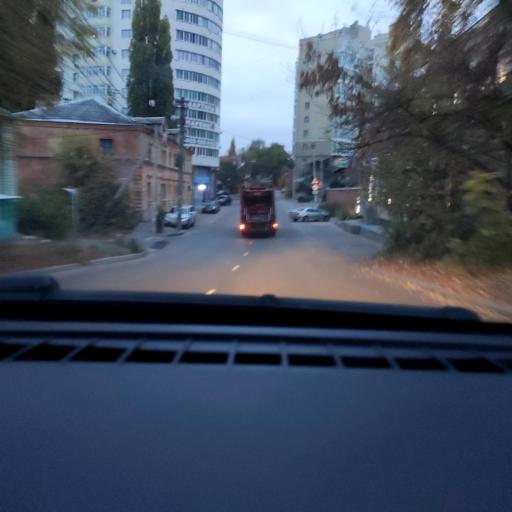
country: RU
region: Voronezj
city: Voronezh
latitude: 51.6704
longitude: 39.2130
